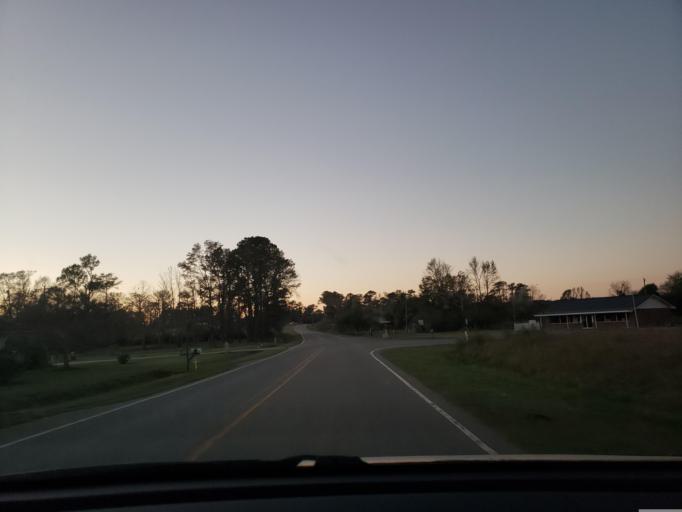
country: US
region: North Carolina
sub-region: Duplin County
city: Beulaville
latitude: 34.8019
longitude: -77.7816
